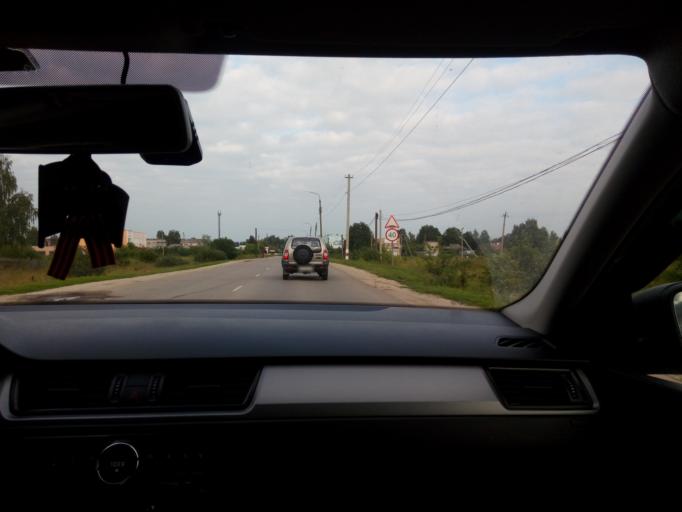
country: RU
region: Nizjnij Novgorod
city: Voskresenskoye
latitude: 56.8387
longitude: 45.4229
